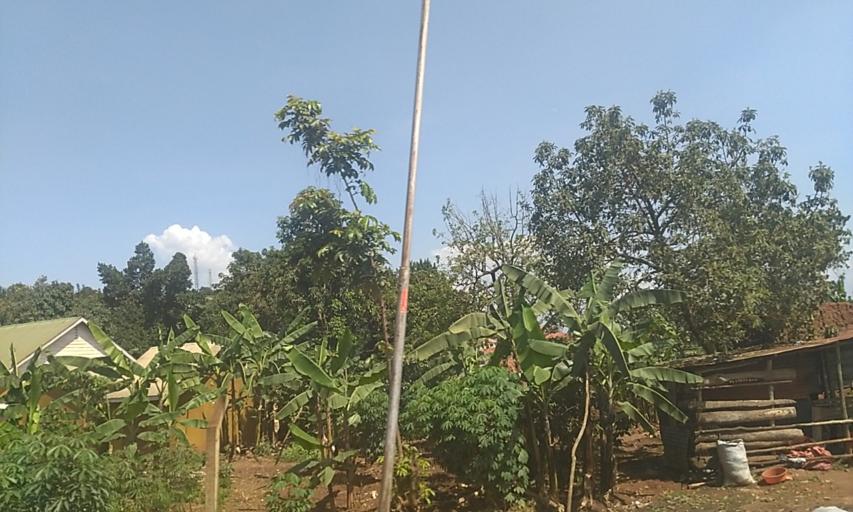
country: UG
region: Central Region
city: Kampala Central Division
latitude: 0.3883
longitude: 32.5930
